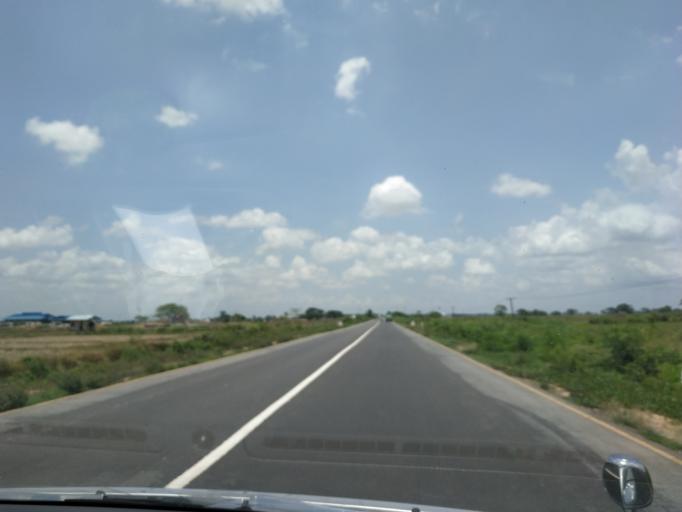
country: MM
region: Bago
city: Thanatpin
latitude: 17.4578
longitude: 96.6038
